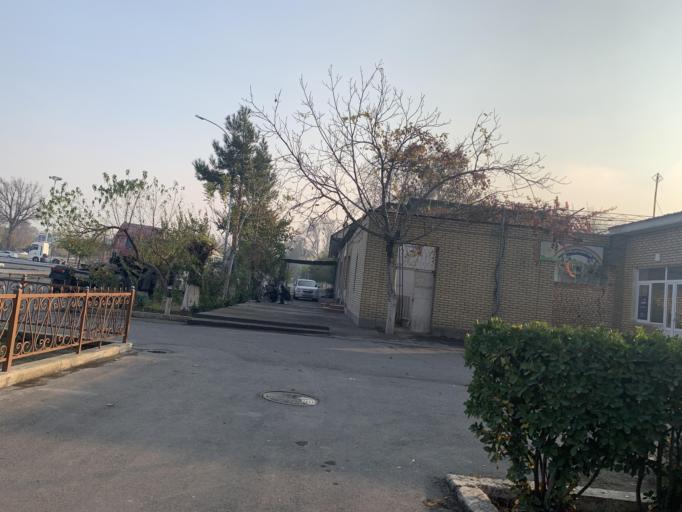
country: UZ
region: Fergana
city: Qo`qon
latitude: 40.5394
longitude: 70.9349
